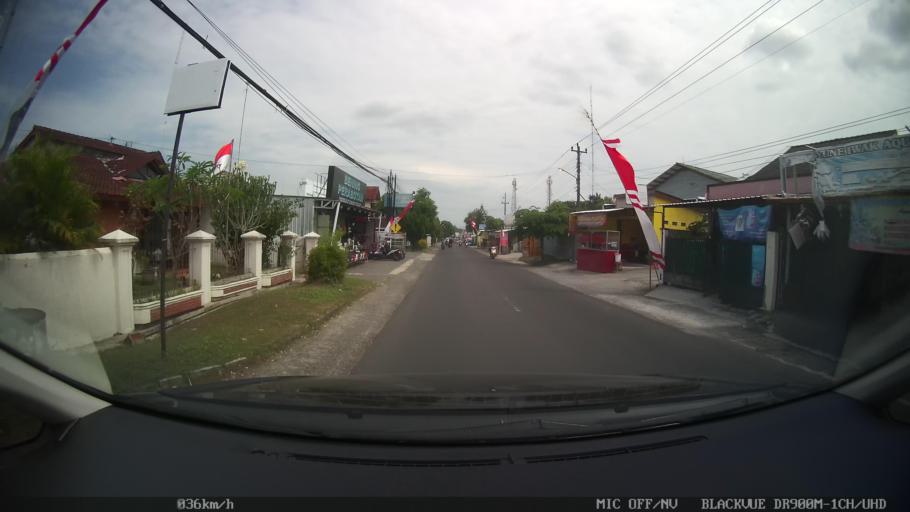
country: ID
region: Daerah Istimewa Yogyakarta
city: Depok
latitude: -7.7436
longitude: 110.4507
